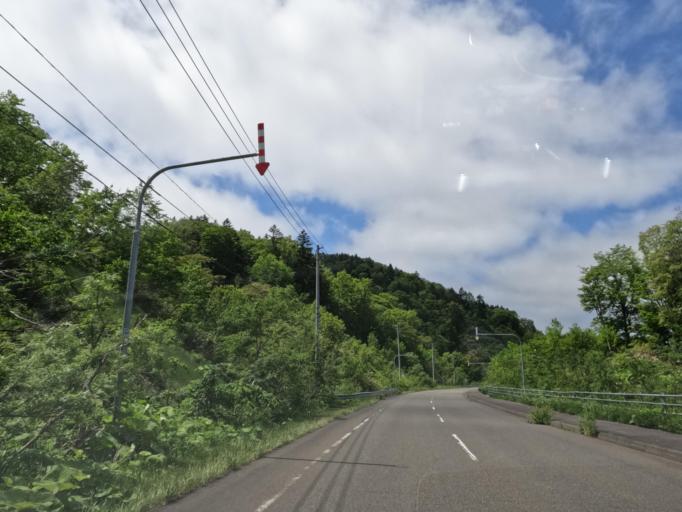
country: JP
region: Hokkaido
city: Tobetsu
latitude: 43.3313
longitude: 141.5703
